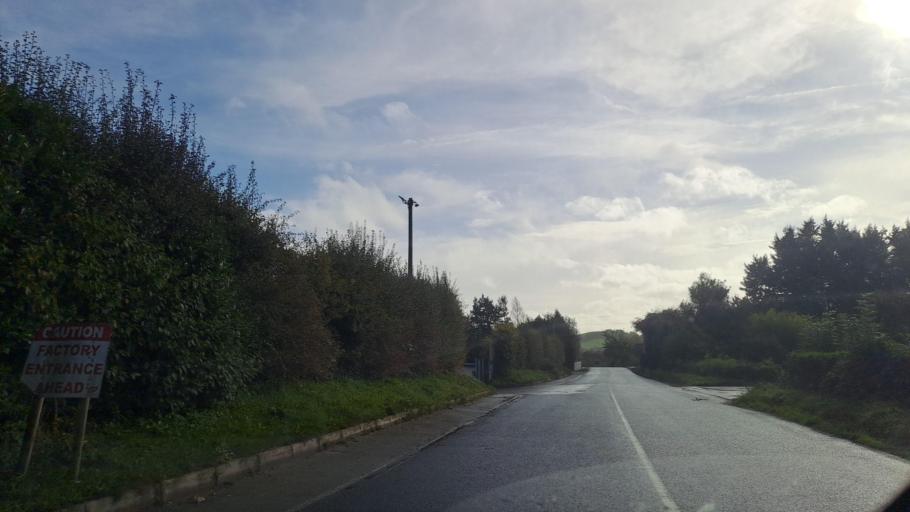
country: IE
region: Ulster
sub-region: County Monaghan
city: Carrickmacross
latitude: 53.9022
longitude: -6.6970
